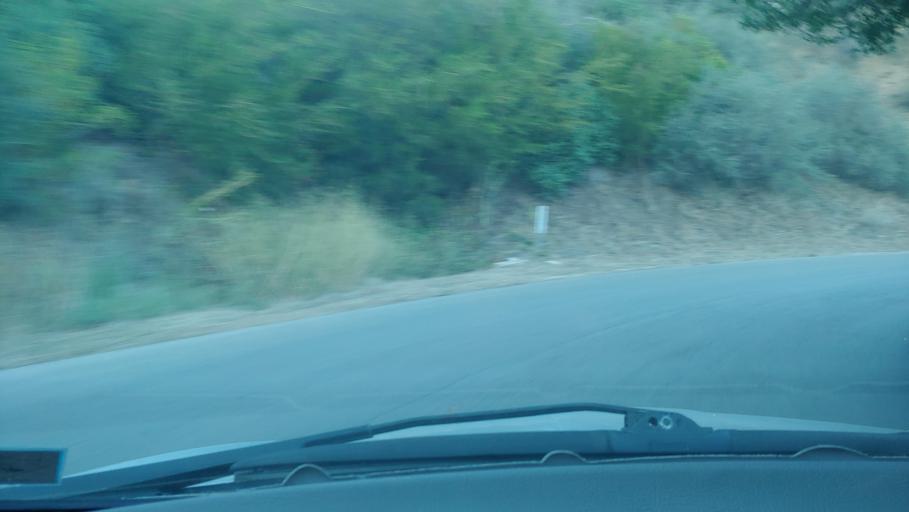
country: US
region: California
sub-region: Santa Barbara County
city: Mission Canyon
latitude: 34.4692
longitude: -119.6747
